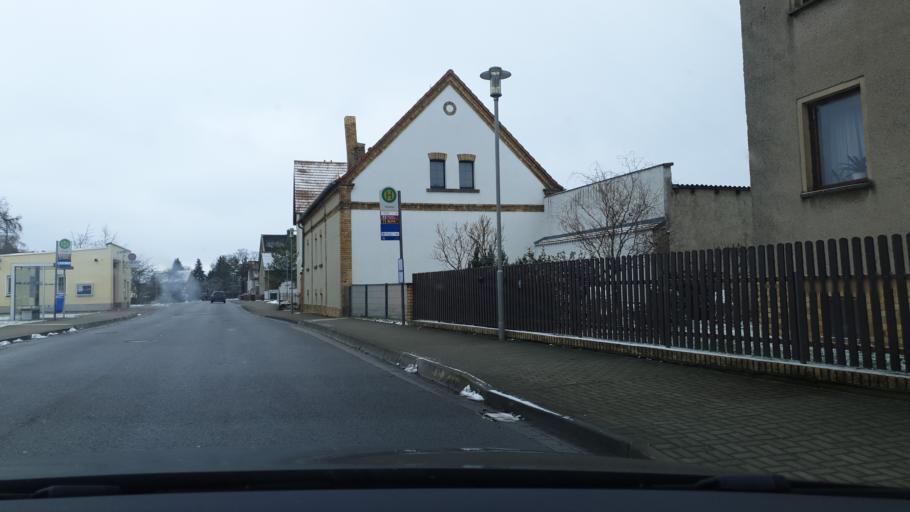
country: DE
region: Saxony
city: Borsdorf
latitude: 51.3100
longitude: 12.5184
